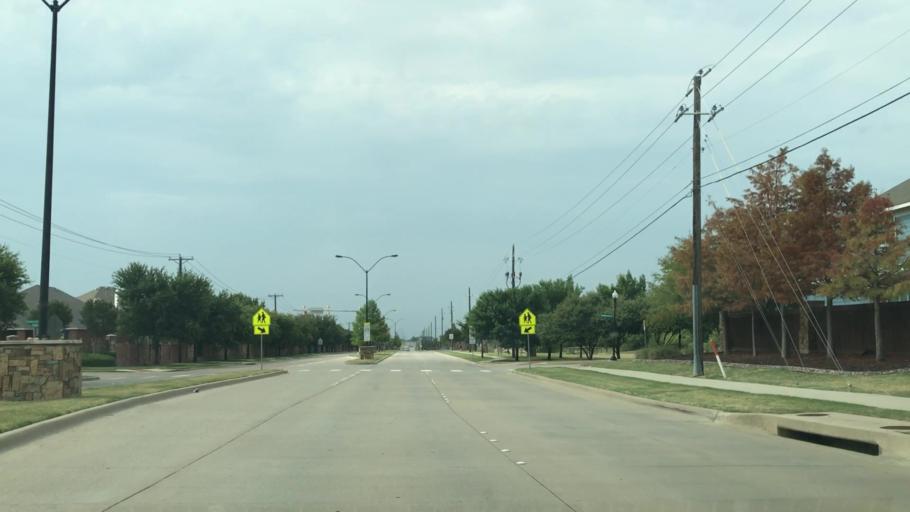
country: US
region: Texas
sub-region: Tarrant County
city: Keller
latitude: 32.9077
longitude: -97.2726
